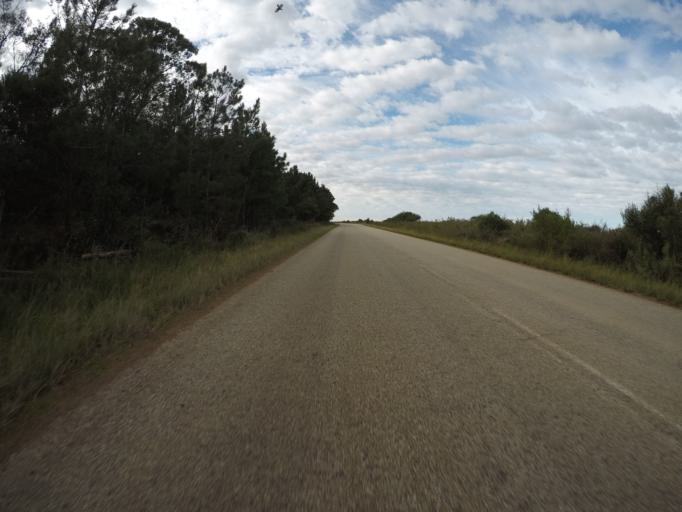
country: ZA
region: Eastern Cape
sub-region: Cacadu District Municipality
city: Kareedouw
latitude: -34.0140
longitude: 24.3002
